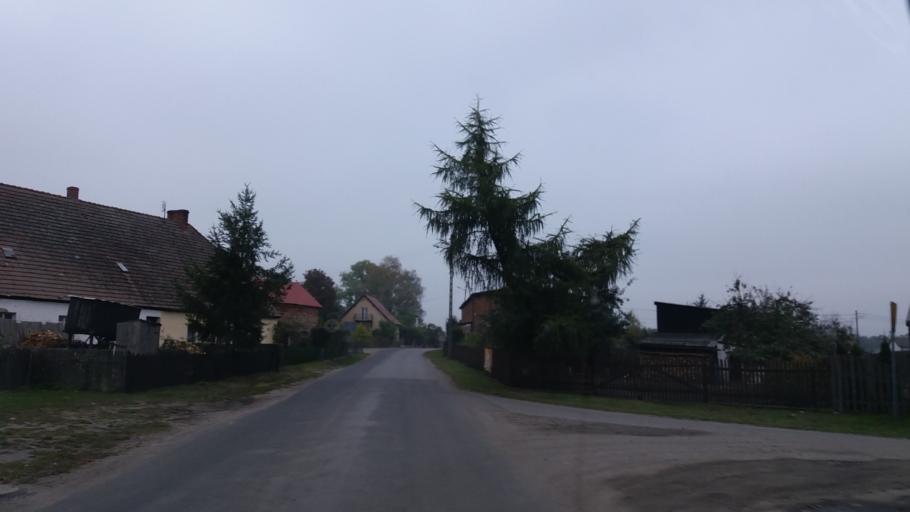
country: PL
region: Lubusz
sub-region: Powiat strzelecko-drezdenecki
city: Dobiegniew
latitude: 53.0510
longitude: 15.7493
